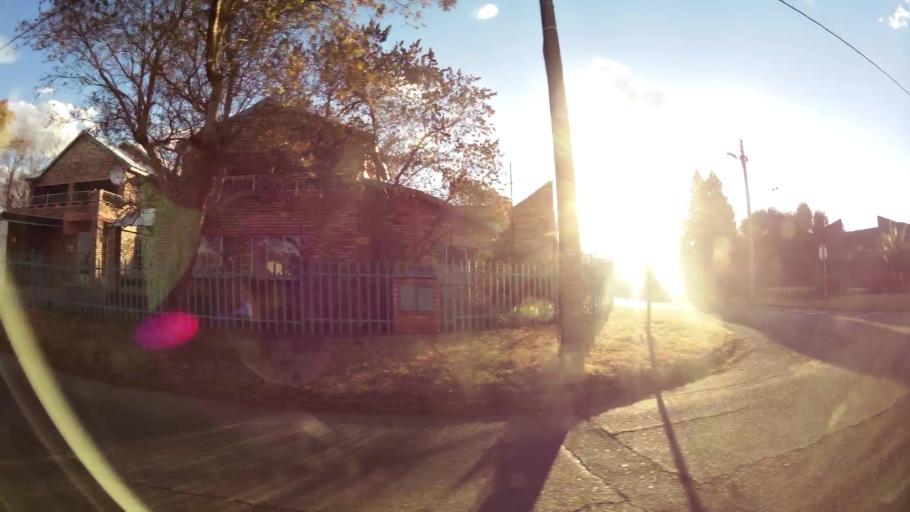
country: ZA
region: North-West
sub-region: Dr Kenneth Kaunda District Municipality
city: Potchefstroom
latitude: -26.7303
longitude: 27.0998
